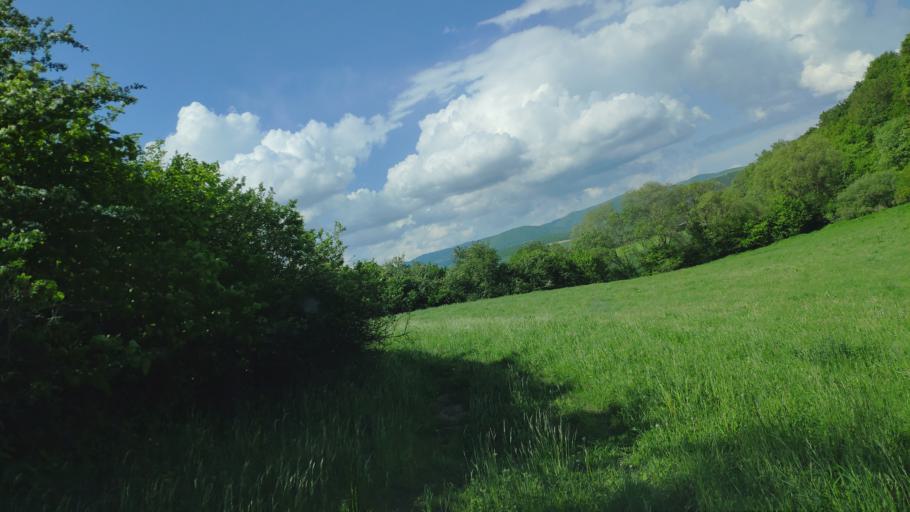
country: SK
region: Presovsky
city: Sabinov
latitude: 49.0541
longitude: 21.1592
